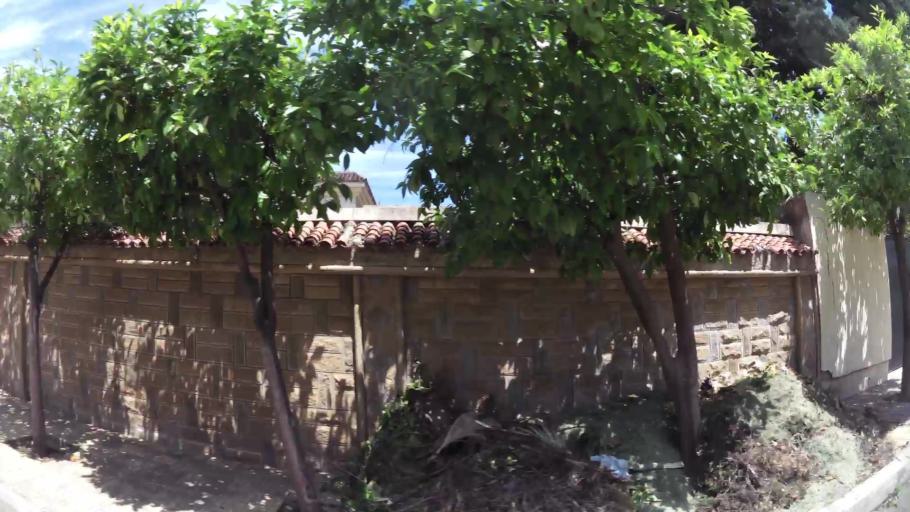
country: MA
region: Fes-Boulemane
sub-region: Fes
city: Fes
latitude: 34.0120
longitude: -4.9938
